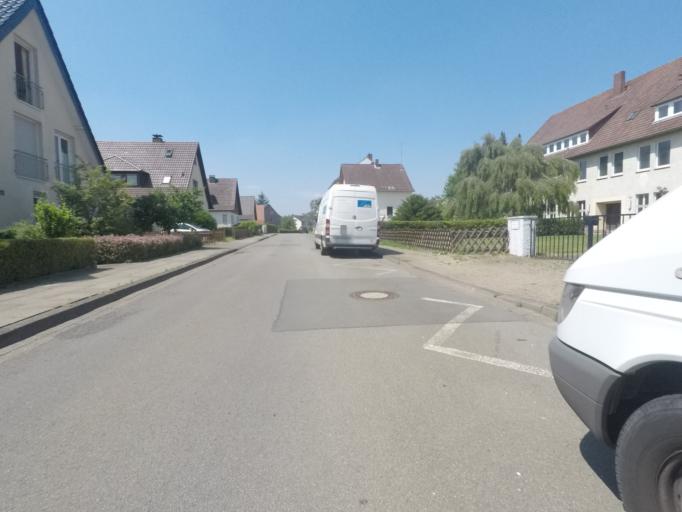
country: DE
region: North Rhine-Westphalia
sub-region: Regierungsbezirk Detmold
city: Bielefeld
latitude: 52.0193
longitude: 8.5725
